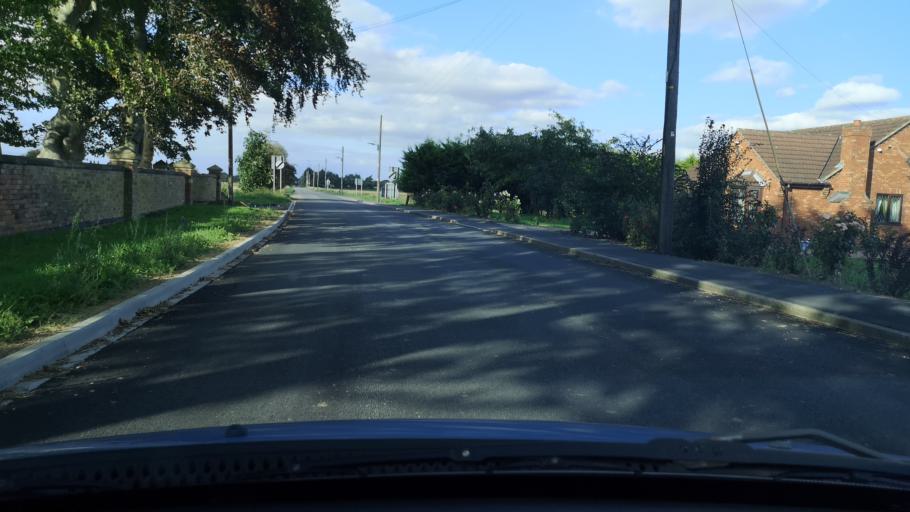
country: GB
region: England
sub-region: North Lincolnshire
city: Gunness
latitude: 53.5793
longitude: -0.7386
